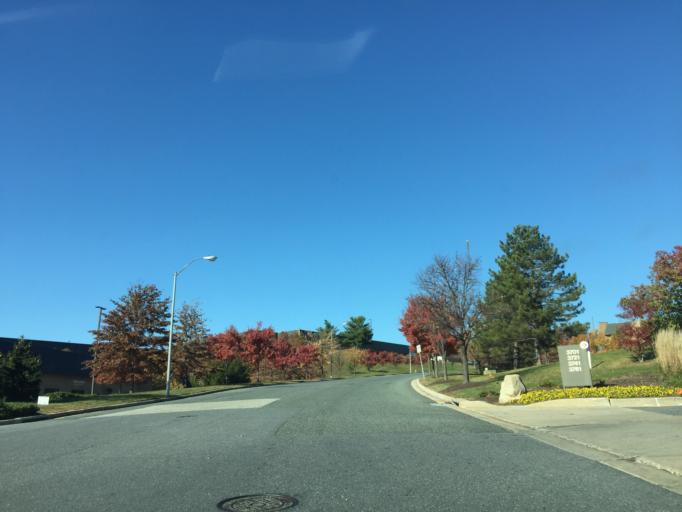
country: US
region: Maryland
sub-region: Baltimore County
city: Lansdowne
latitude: 39.2498
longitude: -76.6734
